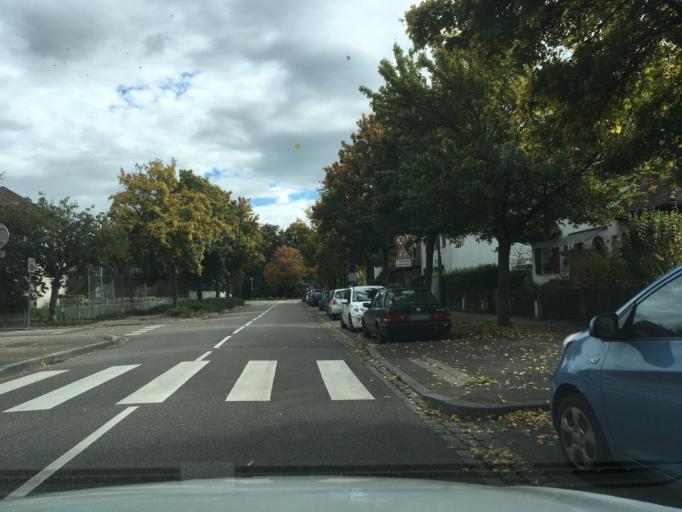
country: FR
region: Alsace
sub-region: Departement du Bas-Rhin
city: Illkirch-Graffenstaden
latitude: 48.5326
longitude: 7.7722
